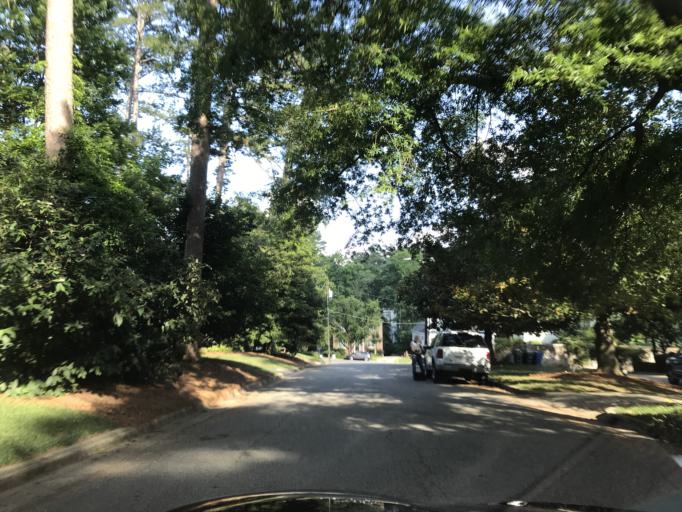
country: US
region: North Carolina
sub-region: Wake County
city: West Raleigh
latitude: 35.8077
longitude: -78.6666
